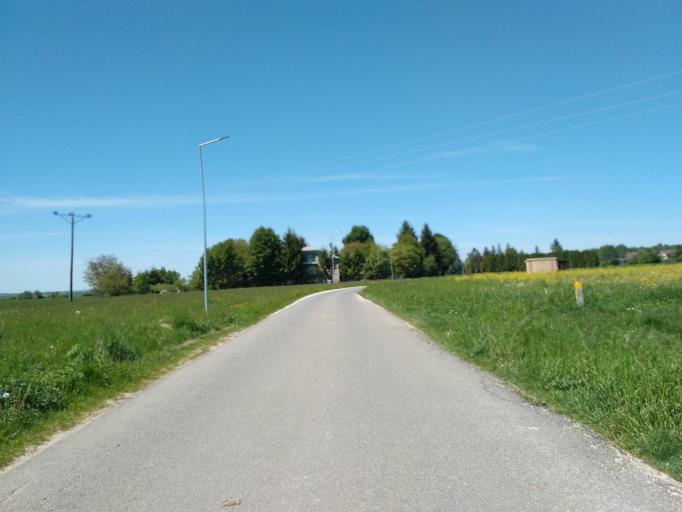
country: PL
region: Subcarpathian Voivodeship
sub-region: Powiat sanocki
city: Dlugie
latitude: 49.5962
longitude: 22.0449
